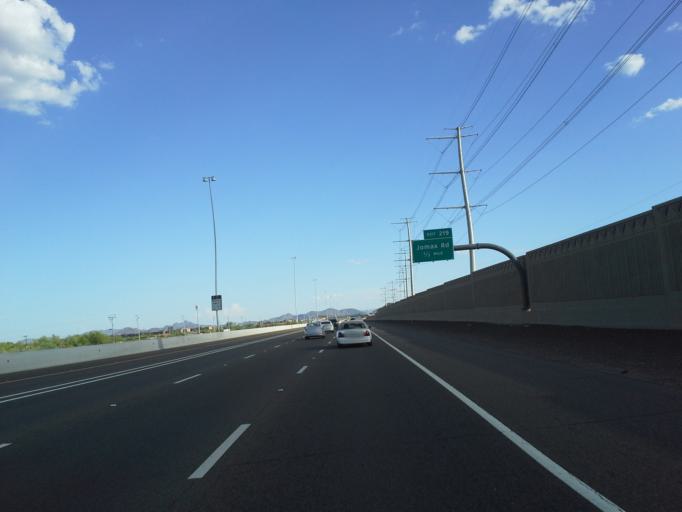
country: US
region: Arizona
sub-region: Maricopa County
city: Anthem
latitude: 33.7406
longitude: -112.1235
